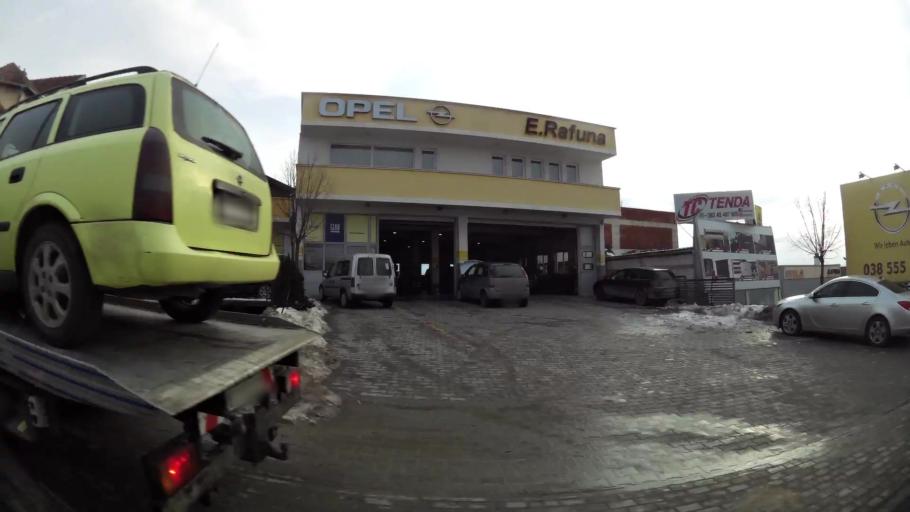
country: XK
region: Pristina
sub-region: Komuna e Prishtines
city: Pristina
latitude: 42.6300
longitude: 21.1564
